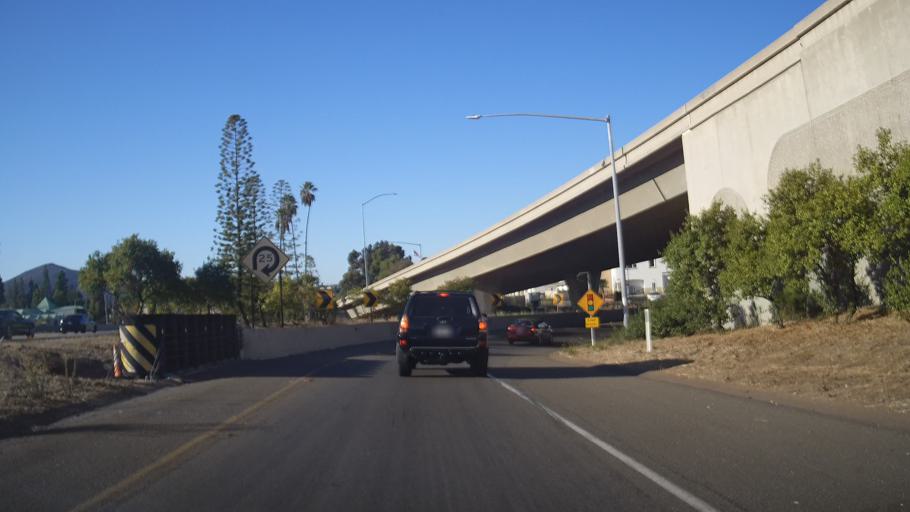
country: US
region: California
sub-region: San Diego County
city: La Mesa
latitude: 32.7792
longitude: -117.0038
